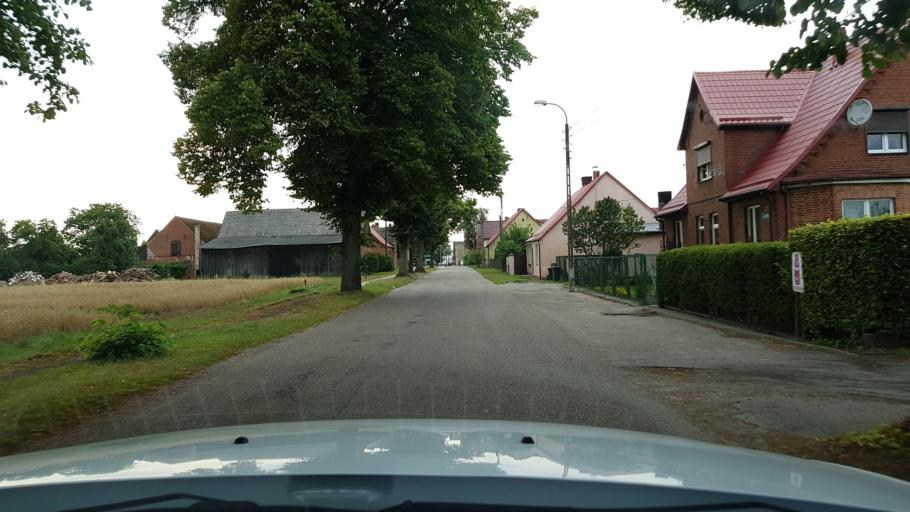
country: PL
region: West Pomeranian Voivodeship
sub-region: Powiat drawski
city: Wierzchowo
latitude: 53.4577
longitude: 16.1069
